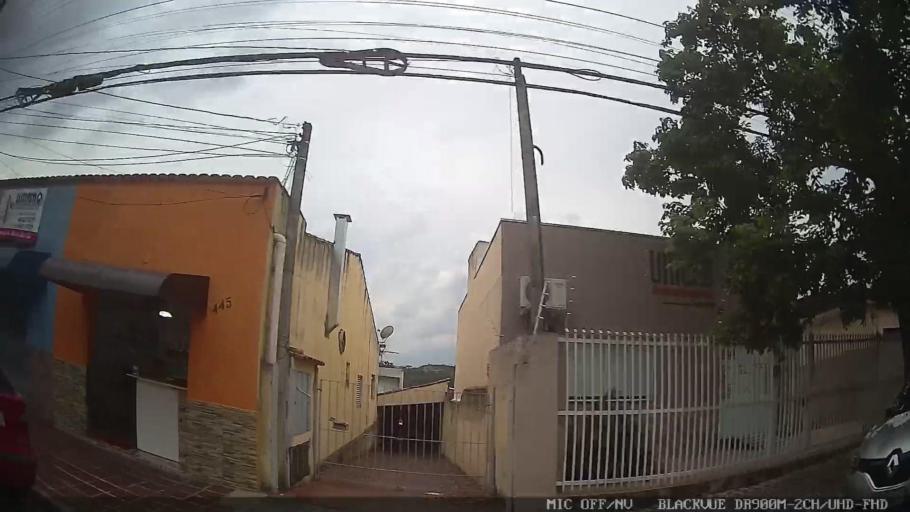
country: BR
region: Sao Paulo
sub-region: Atibaia
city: Atibaia
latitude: -23.1198
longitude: -46.5639
